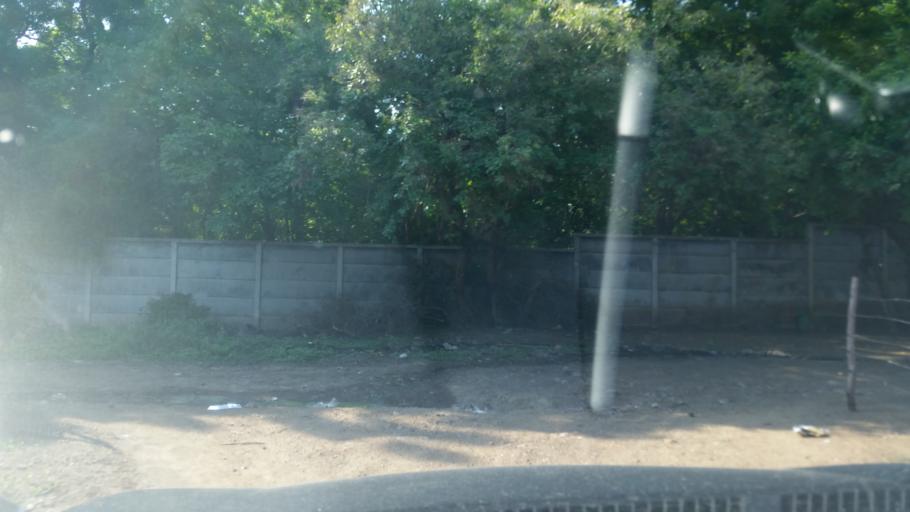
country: NI
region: Managua
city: Masachapa
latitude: 11.7903
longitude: -86.5150
